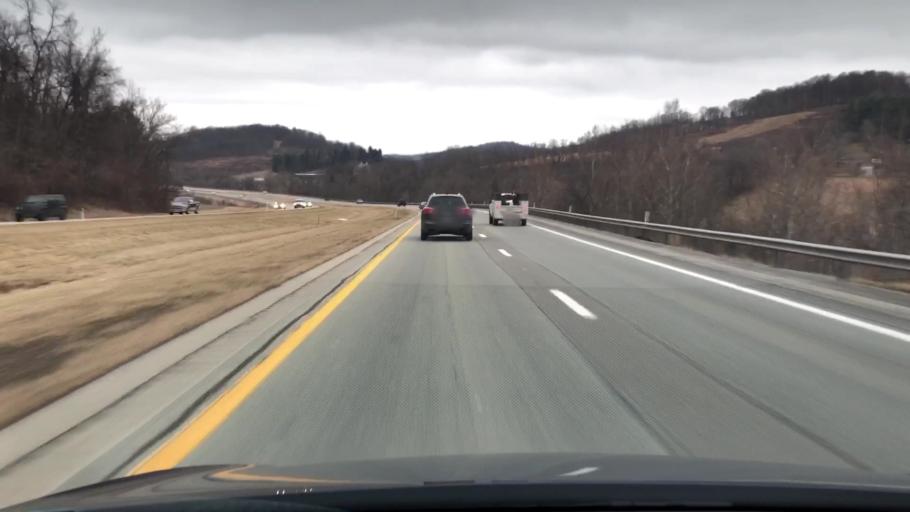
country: US
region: Pennsylvania
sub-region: Washington County
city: East Washington
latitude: 40.0938
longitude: -80.1930
